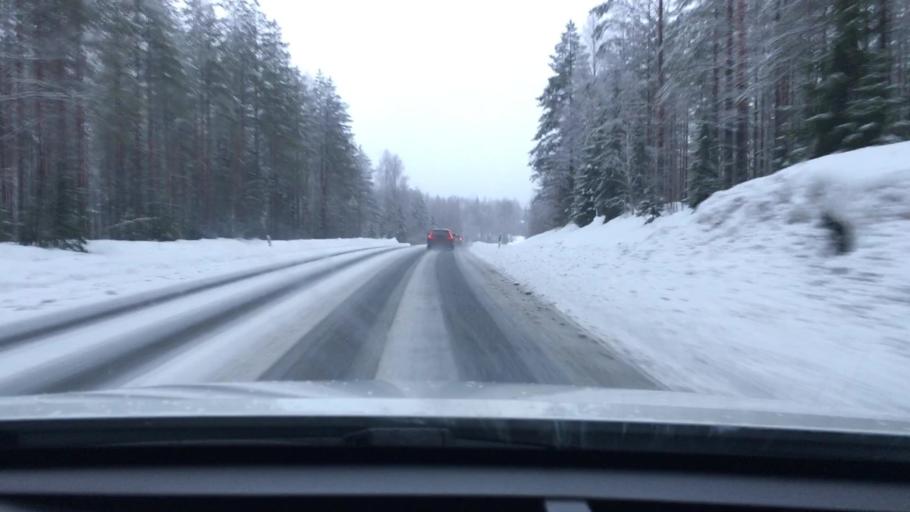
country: FI
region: Northern Savo
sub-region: Ylae-Savo
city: Sonkajaervi
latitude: 63.7654
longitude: 27.4113
